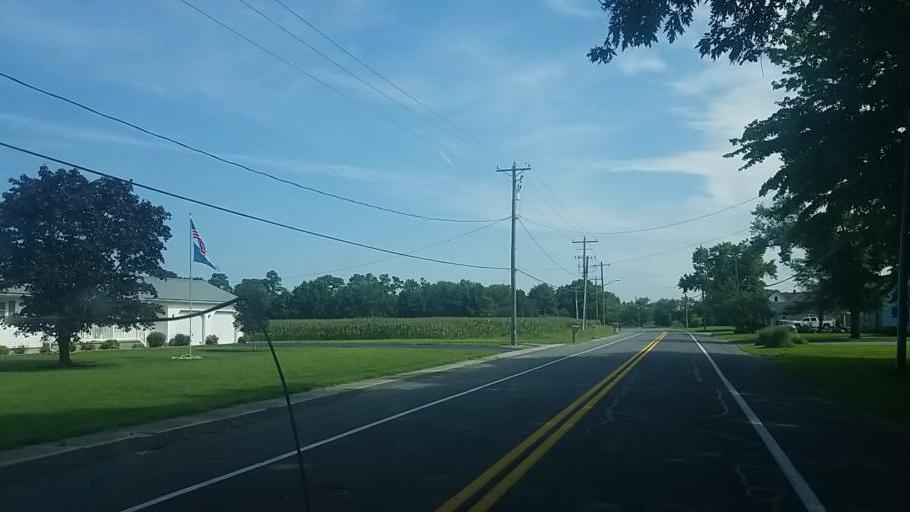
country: US
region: Delaware
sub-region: Sussex County
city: Selbyville
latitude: 38.5284
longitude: -75.2364
